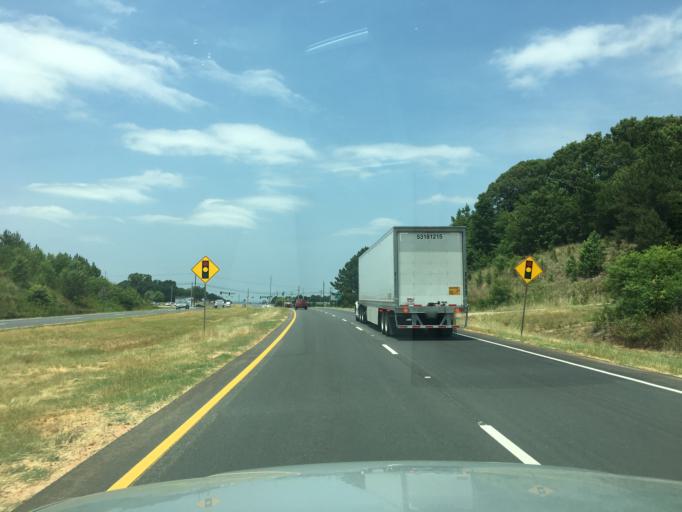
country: US
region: Georgia
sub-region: Jackson County
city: Commerce
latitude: 34.2315
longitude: -83.4510
